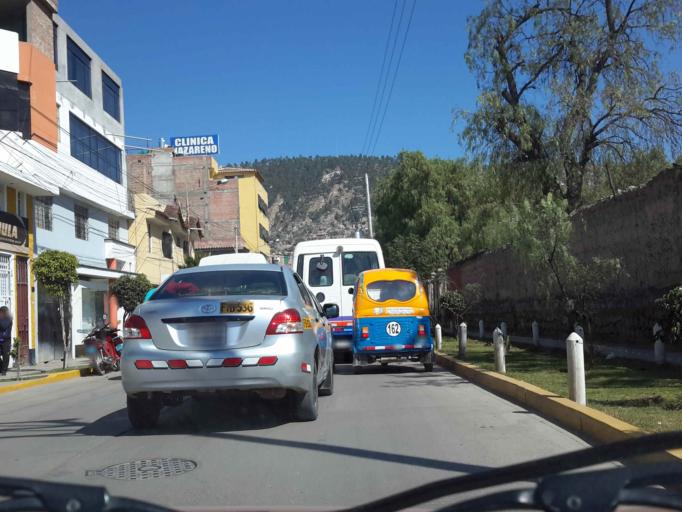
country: PE
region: Ayacucho
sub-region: Provincia de Huamanga
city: Ayacucho
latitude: -13.1555
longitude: -74.2222
